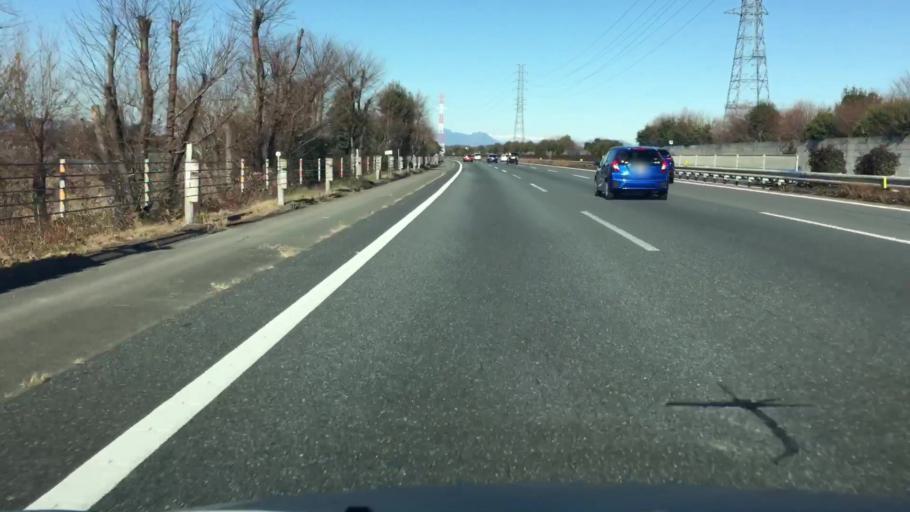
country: JP
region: Saitama
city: Yorii
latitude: 36.1539
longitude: 139.2173
